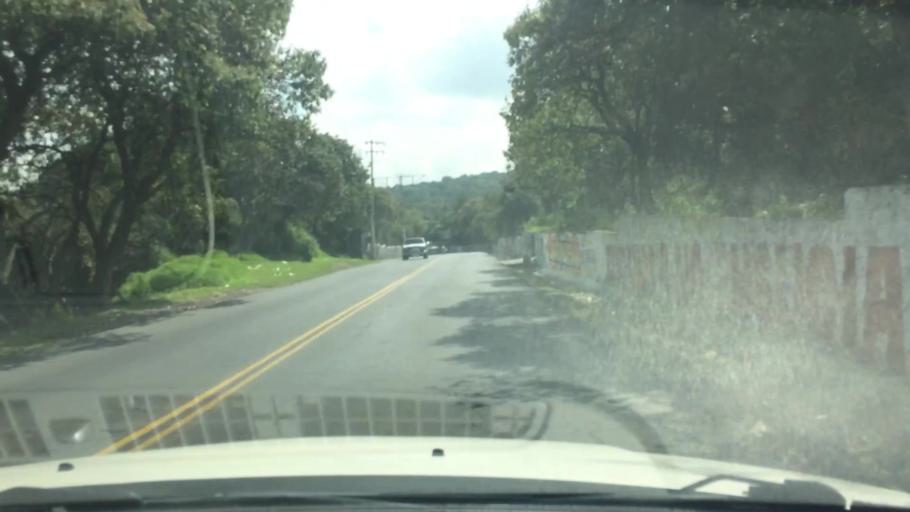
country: MX
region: Mexico City
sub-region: Tlalpan
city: Lomas de Tepemecatl
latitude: 19.2668
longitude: -99.2300
